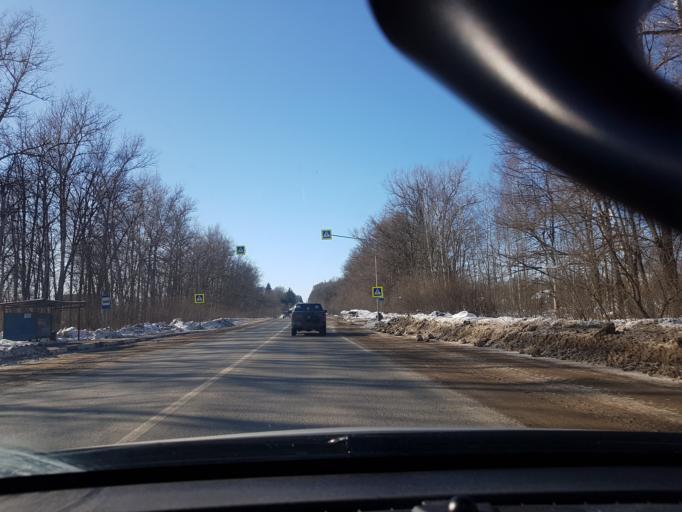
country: RU
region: Moskovskaya
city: Kostrovo
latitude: 55.9103
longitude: 36.7746
